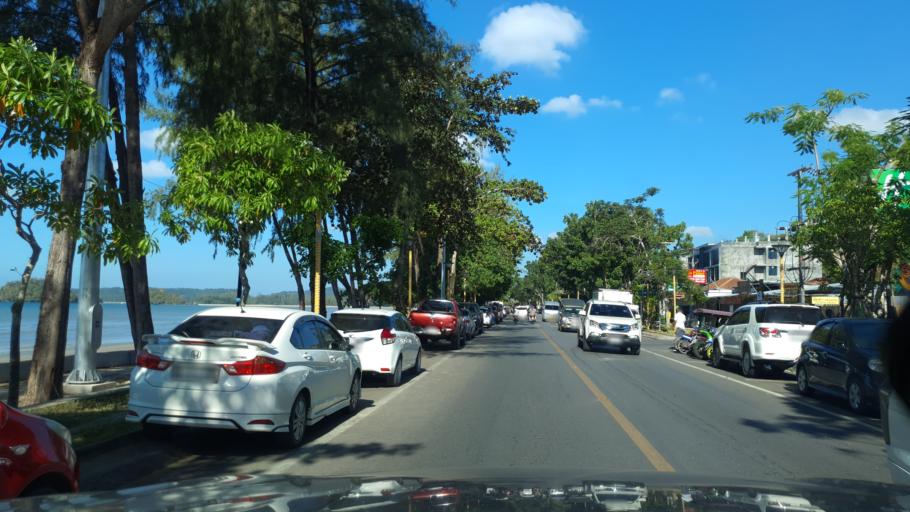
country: TH
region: Phangnga
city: Ban Ao Nang
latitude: 8.0402
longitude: 98.8144
